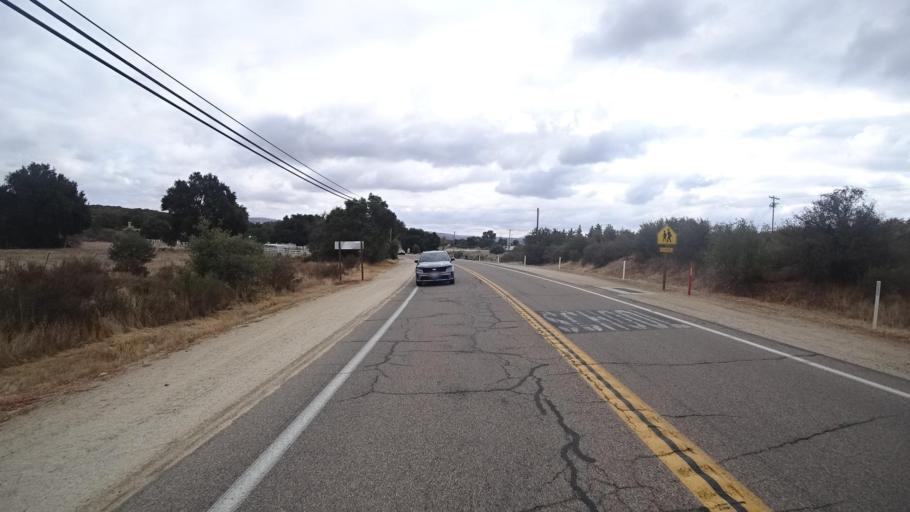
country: US
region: California
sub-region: San Diego County
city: Campo
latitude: 32.6450
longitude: -116.4868
